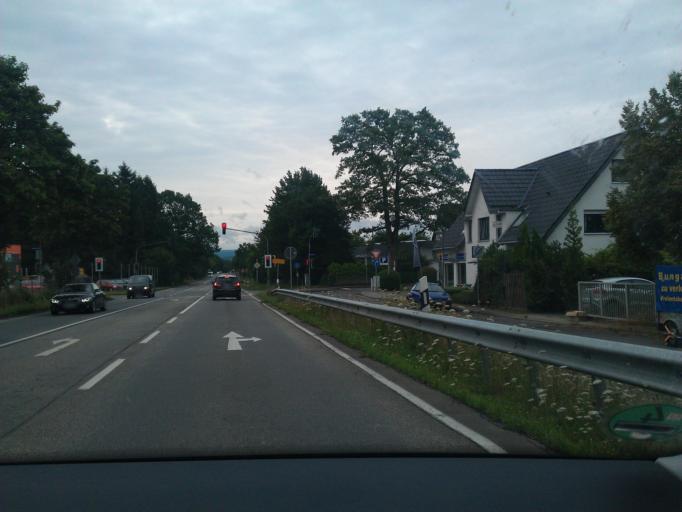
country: BE
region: Wallonia
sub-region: Province de Liege
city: Raeren
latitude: 50.7140
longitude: 6.1338
